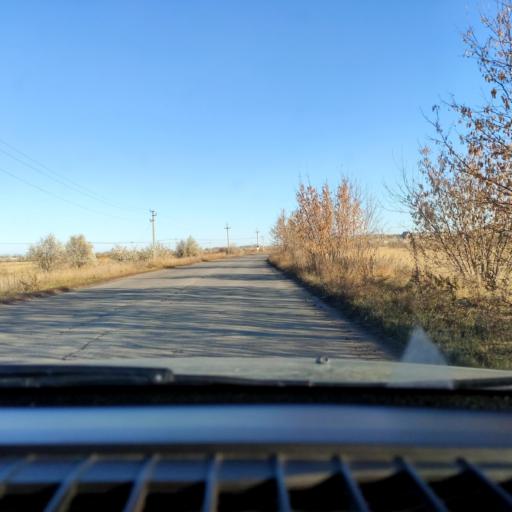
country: RU
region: Samara
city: Tol'yatti
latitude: 53.6429
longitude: 49.3158
